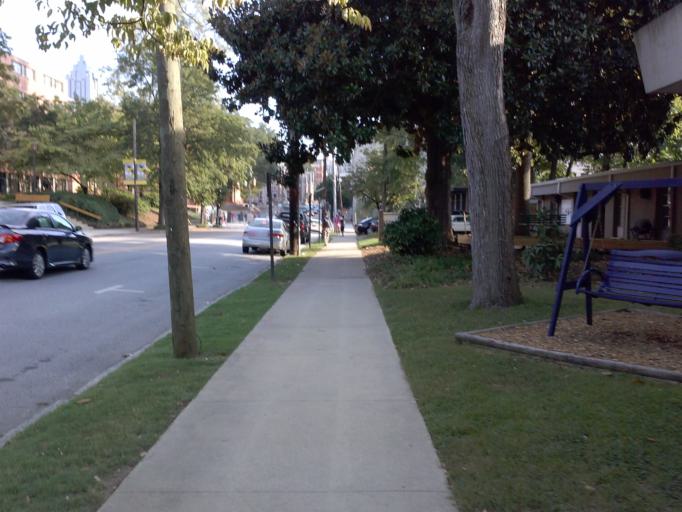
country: US
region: Georgia
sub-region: Fulton County
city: Atlanta
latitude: 33.7748
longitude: -84.3921
